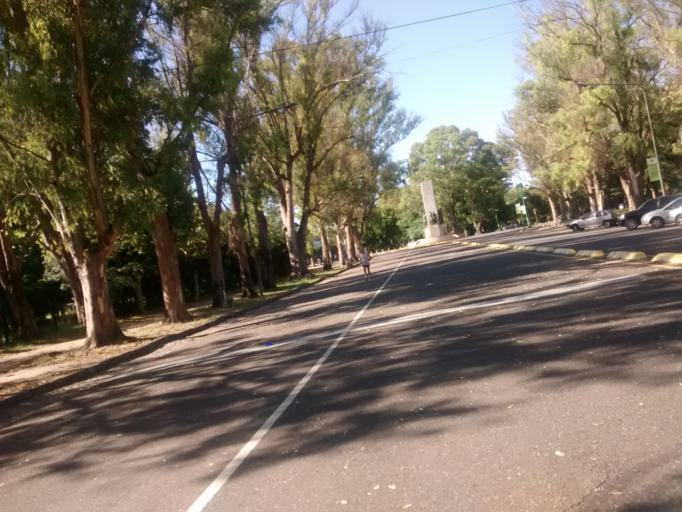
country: AR
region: Buenos Aires
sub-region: Partido de La Plata
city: La Plata
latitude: -34.9083
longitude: -57.9336
